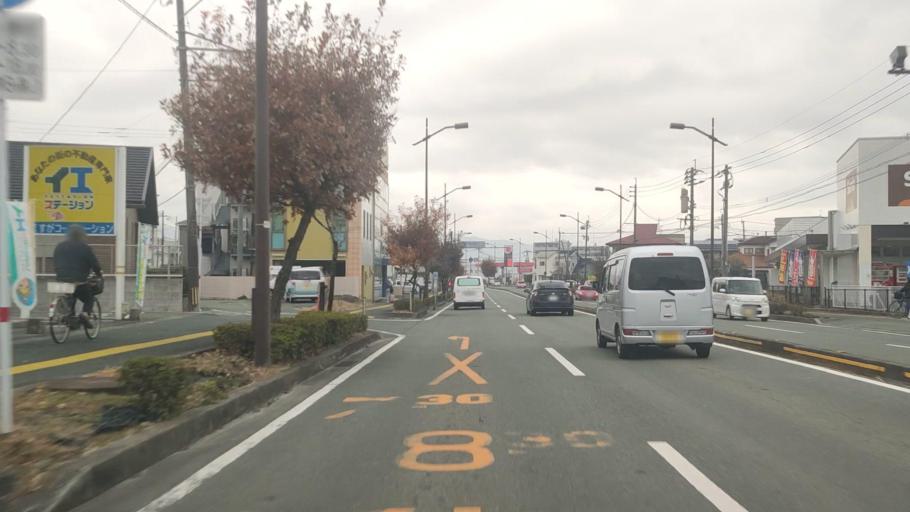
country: JP
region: Kumamoto
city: Kumamoto
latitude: 32.8063
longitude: 130.7524
